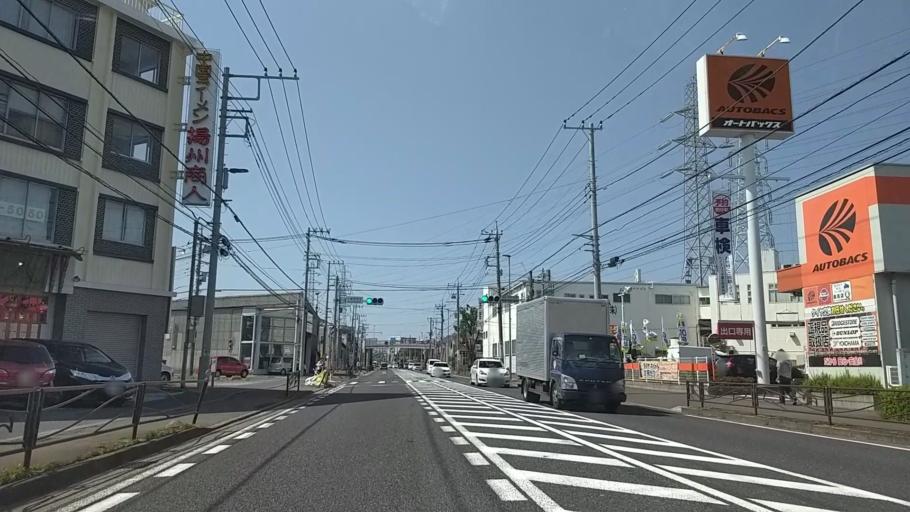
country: JP
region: Kanagawa
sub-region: Kawasaki-shi
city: Kawasaki
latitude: 35.5366
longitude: 139.6656
